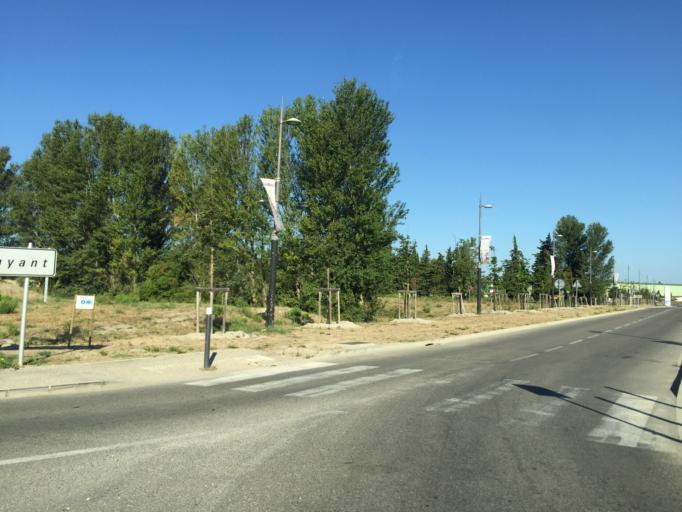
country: FR
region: Provence-Alpes-Cote d'Azur
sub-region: Departement du Vaucluse
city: Althen-des-Paluds
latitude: 44.0246
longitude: 4.9704
